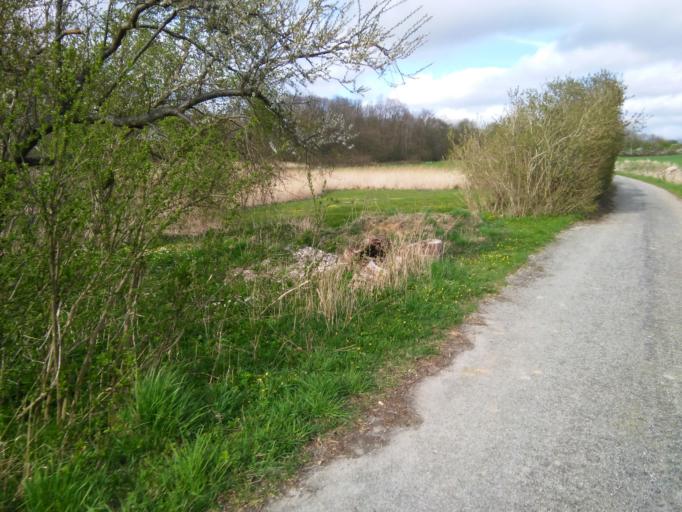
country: DK
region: Central Jutland
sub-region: Arhus Kommune
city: Beder
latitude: 56.0793
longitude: 10.2052
